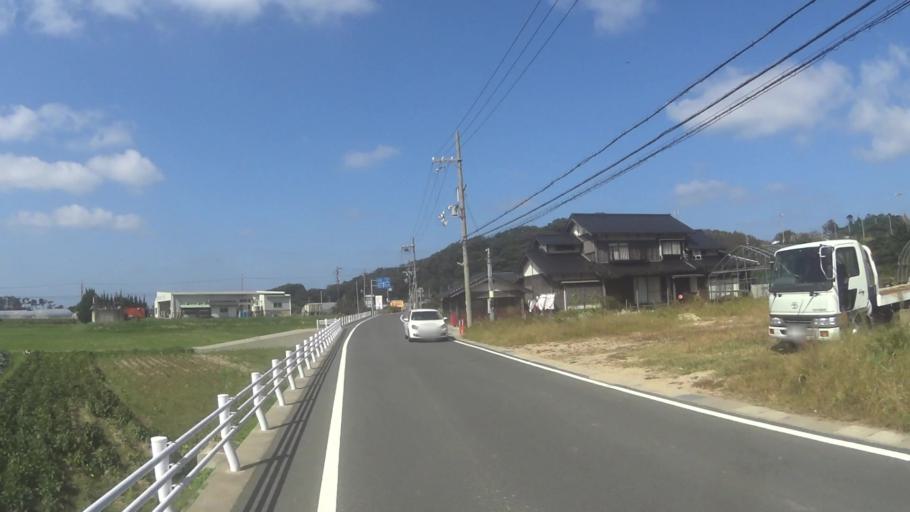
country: JP
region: Kyoto
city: Miyazu
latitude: 35.7388
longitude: 135.1104
